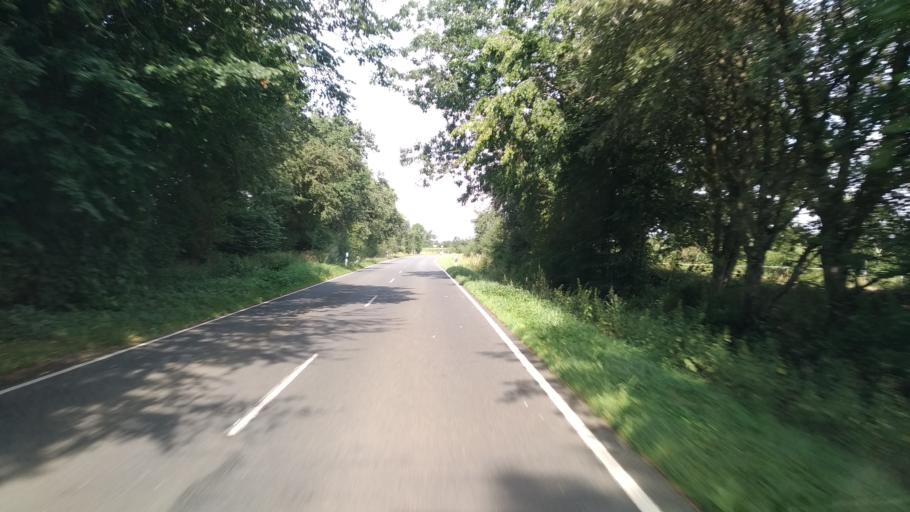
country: DE
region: Schleswig-Holstein
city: Lottorf
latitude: 54.4576
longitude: 9.5851
